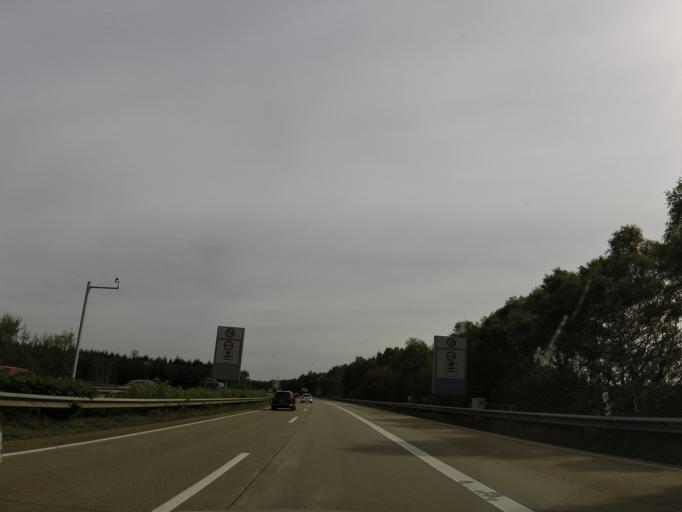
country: DE
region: Lower Saxony
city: Soltau
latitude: 52.9776
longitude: 9.9229
